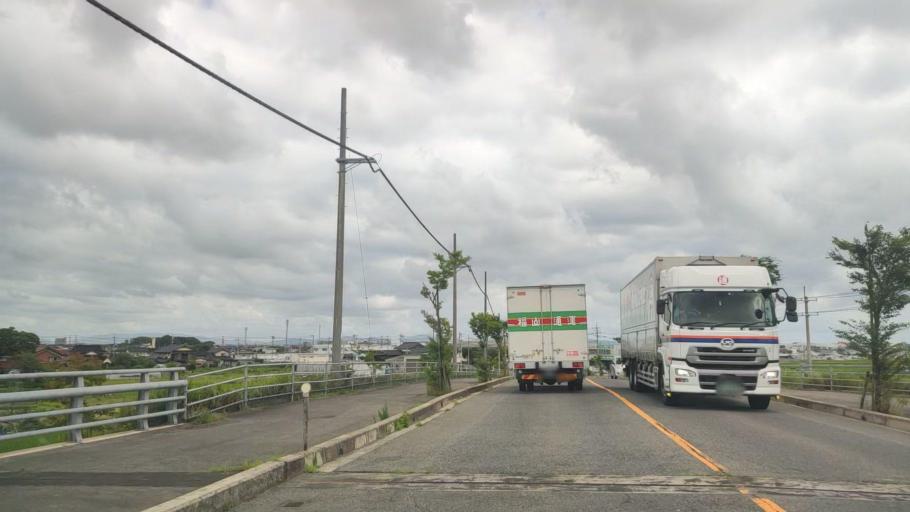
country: JP
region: Tottori
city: Yonago
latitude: 35.4338
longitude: 133.3910
